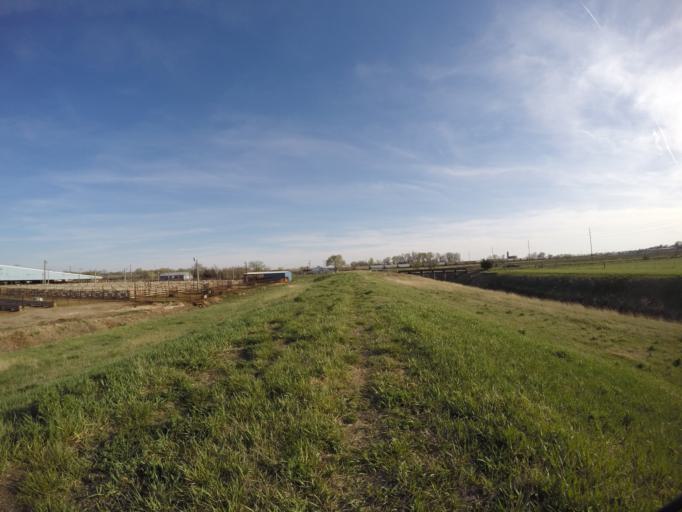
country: US
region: Kansas
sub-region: Saline County
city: Salina
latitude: 38.8465
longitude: -97.6305
